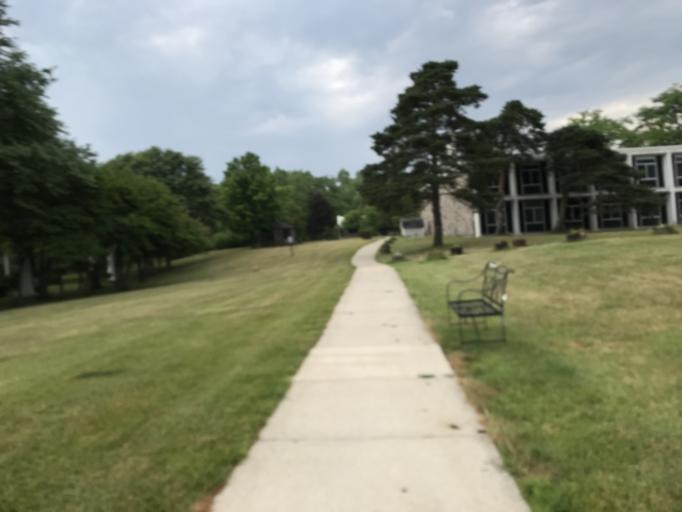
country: US
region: Michigan
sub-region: Oakland County
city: Franklin
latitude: 42.4881
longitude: -83.3331
